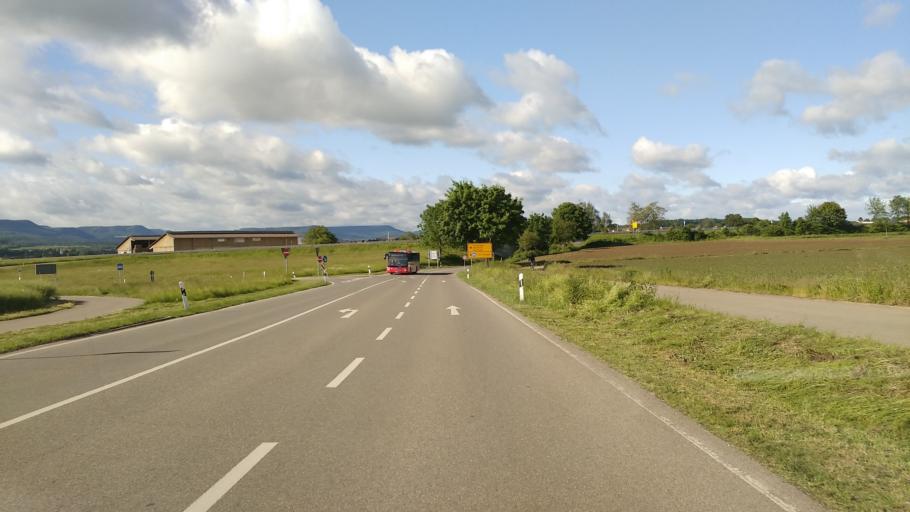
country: DE
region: Baden-Wuerttemberg
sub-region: Tuebingen Region
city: Kusterdingen
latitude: 48.5083
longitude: 9.1108
